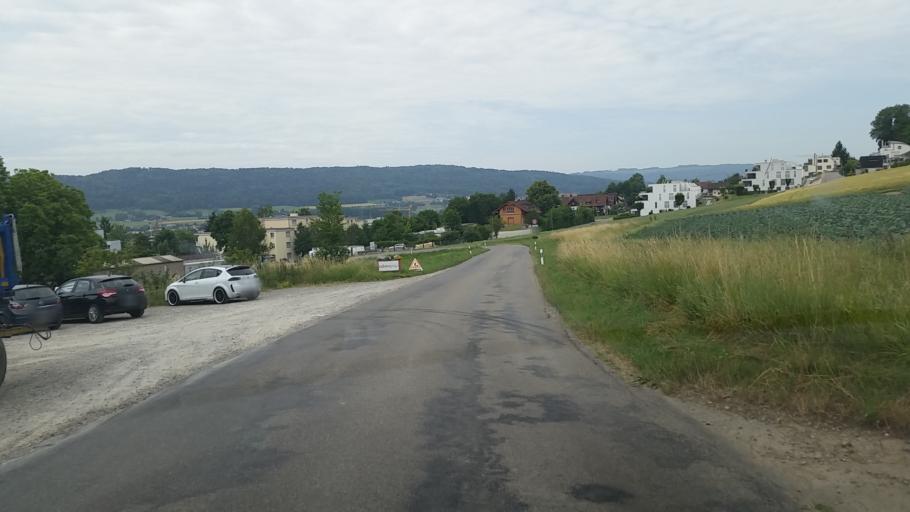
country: CH
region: Zurich
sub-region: Bezirk Dielsdorf
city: Sonnhalde
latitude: 47.4617
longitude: 8.4435
